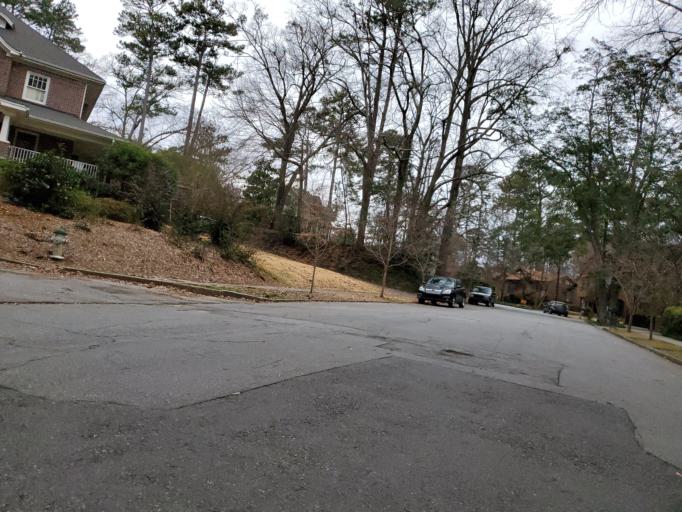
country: US
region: Georgia
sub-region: DeKalb County
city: North Decatur
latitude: 33.7858
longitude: -84.2961
